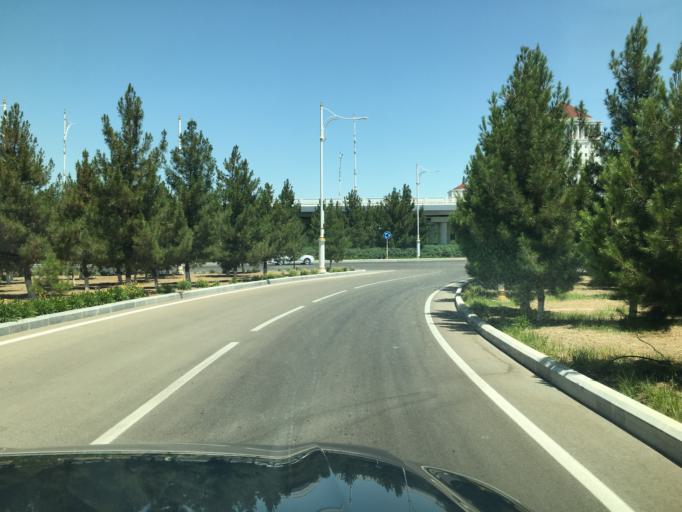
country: TM
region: Ahal
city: Ashgabat
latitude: 37.8779
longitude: 58.3871
